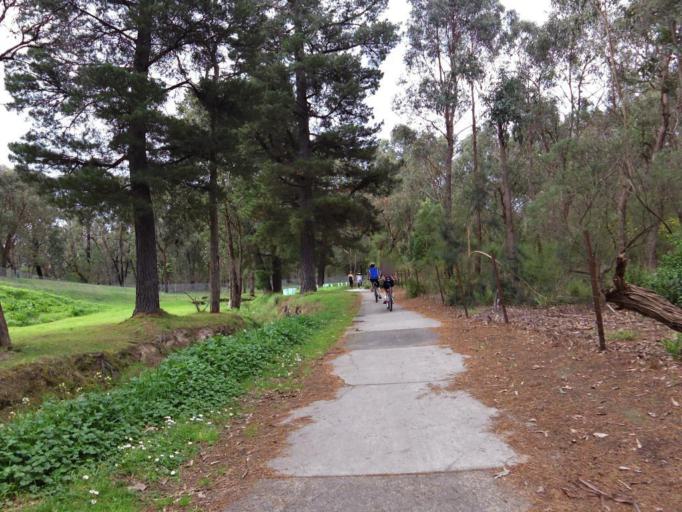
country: AU
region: Victoria
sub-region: Maroondah
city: Croydon Hills
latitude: -37.7855
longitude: 145.2613
